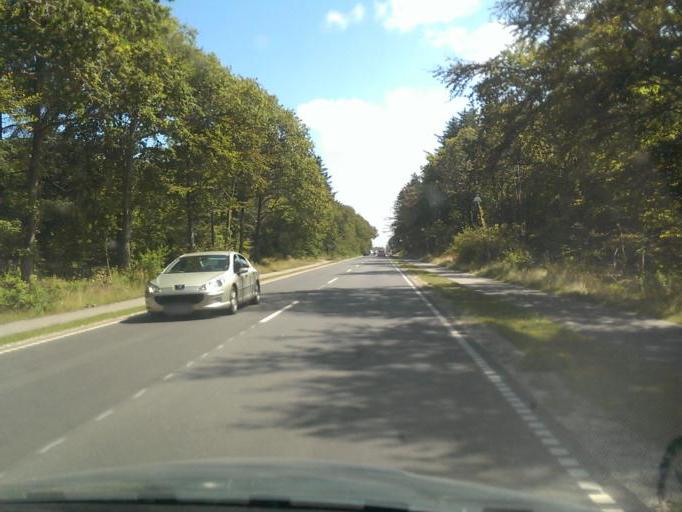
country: DK
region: North Denmark
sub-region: Jammerbugt Kommune
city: Pandrup
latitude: 57.2496
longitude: 9.6052
